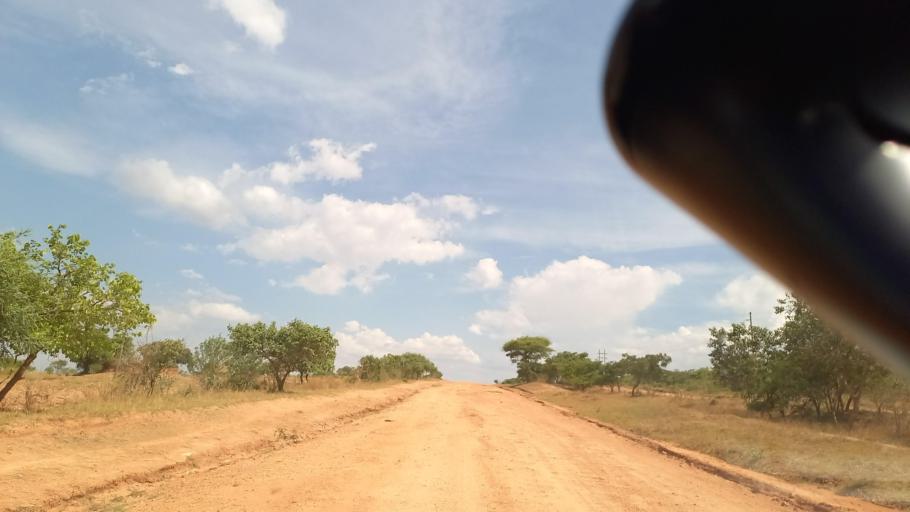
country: ZM
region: Lusaka
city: Kafue
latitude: -16.1287
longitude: 28.0461
